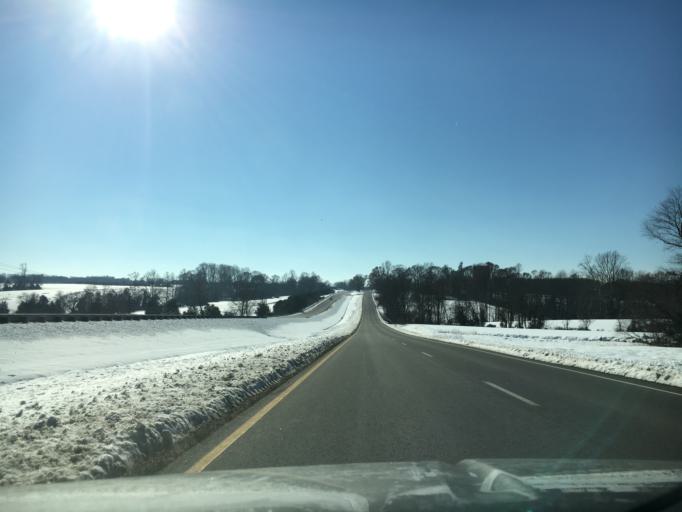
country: US
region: Virginia
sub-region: Nottoway County
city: Crewe
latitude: 37.2704
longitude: -78.1263
